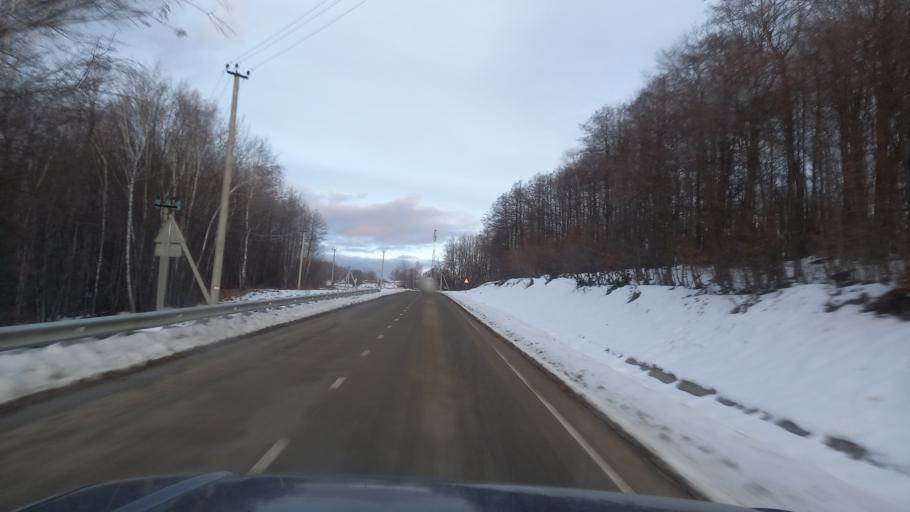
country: RU
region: Adygeya
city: Kamennomostskiy
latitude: 44.2211
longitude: 39.9891
